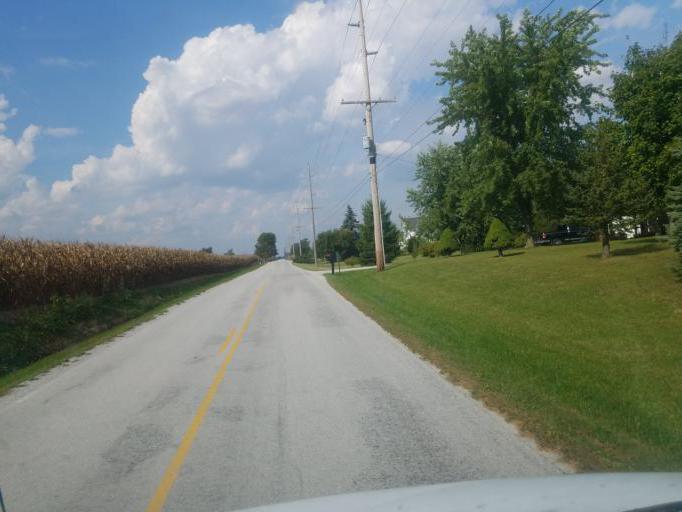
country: US
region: Ohio
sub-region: Hardin County
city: Kenton
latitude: 40.7545
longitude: -83.6524
